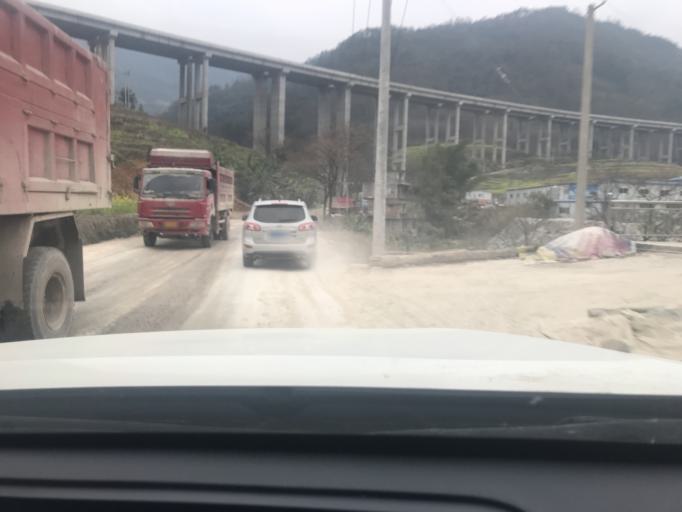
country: CN
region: Guangxi Zhuangzu Zizhiqu
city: Xinzhou
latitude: 25.0080
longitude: 105.8434
